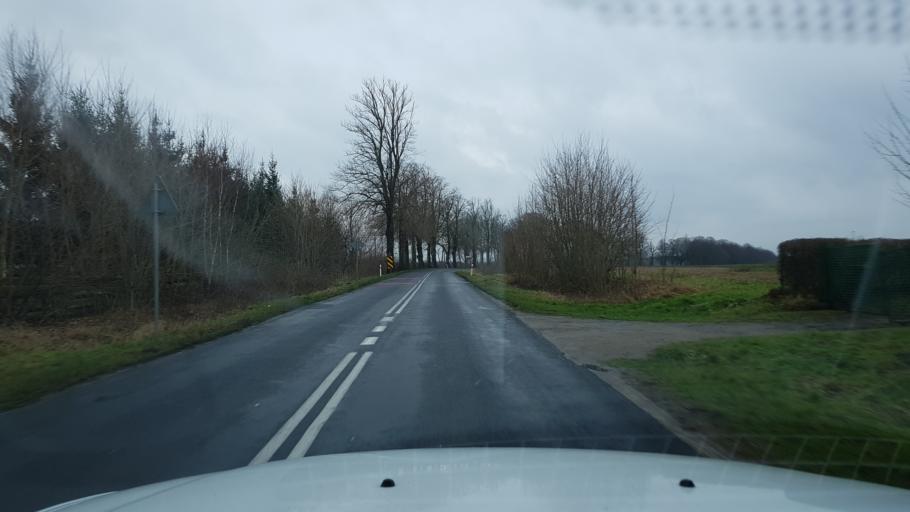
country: PL
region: West Pomeranian Voivodeship
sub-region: Powiat gryficki
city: Brojce
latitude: 54.0602
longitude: 15.3874
